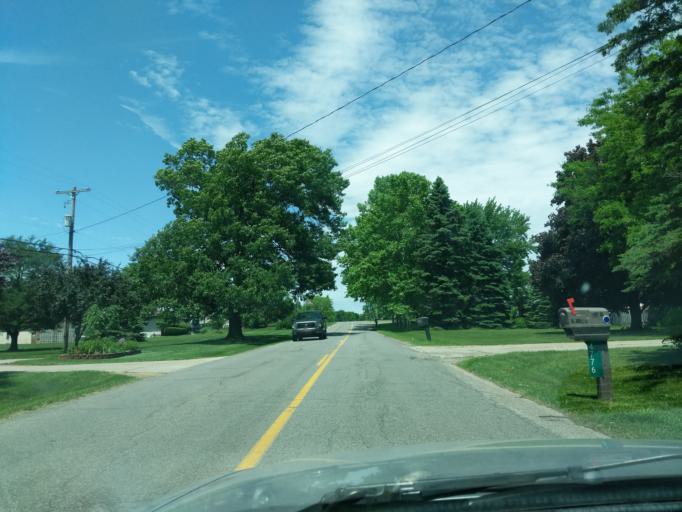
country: US
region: Michigan
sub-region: Jackson County
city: Michigan Center
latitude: 42.1915
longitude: -84.3070
